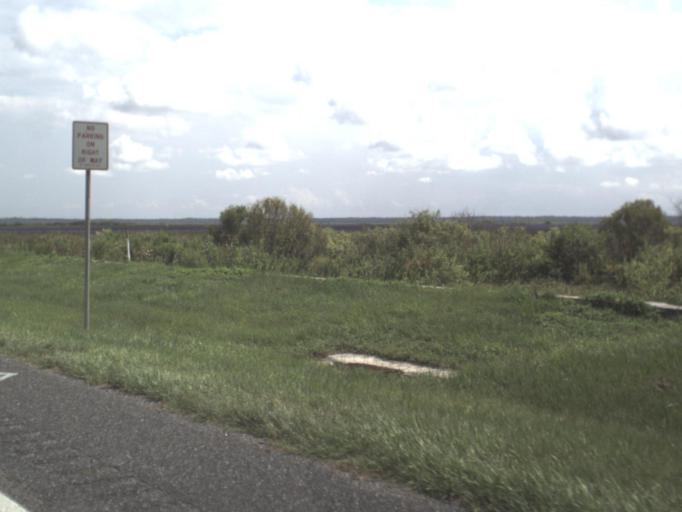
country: US
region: Florida
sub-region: Alachua County
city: Gainesville
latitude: 29.5638
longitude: -82.3325
